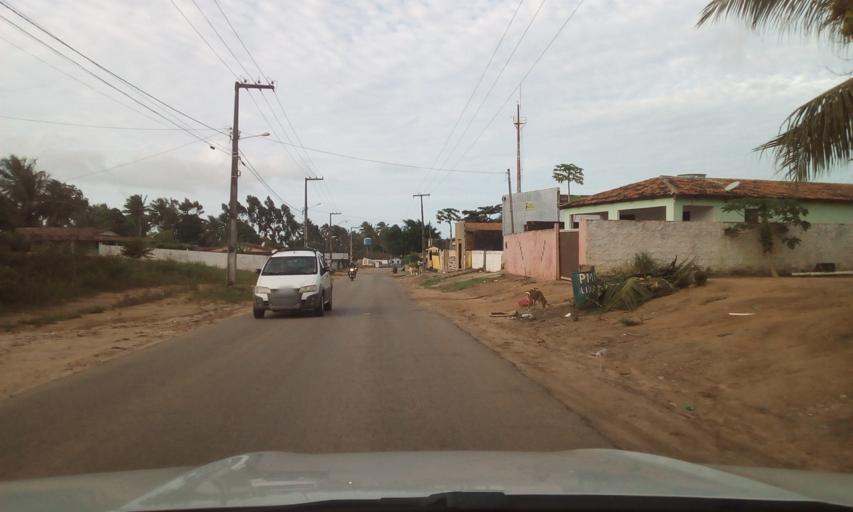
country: BR
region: Paraiba
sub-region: Conde
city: Conde
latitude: -7.2688
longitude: -34.8492
